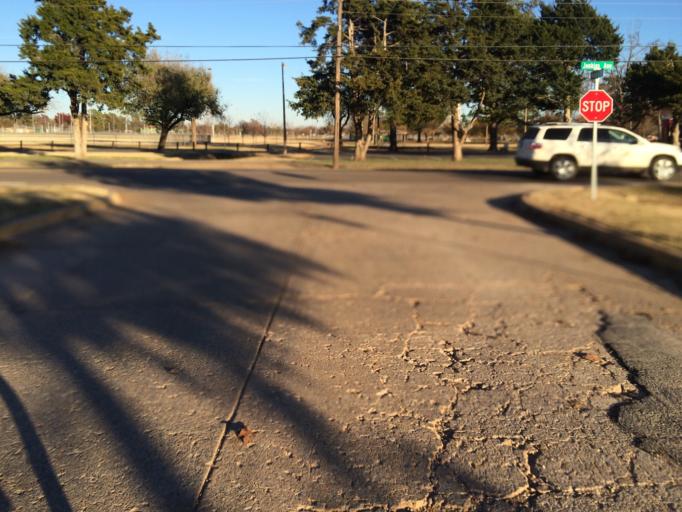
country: US
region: Oklahoma
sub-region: Cleveland County
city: Norman
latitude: 35.1944
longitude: -97.4416
